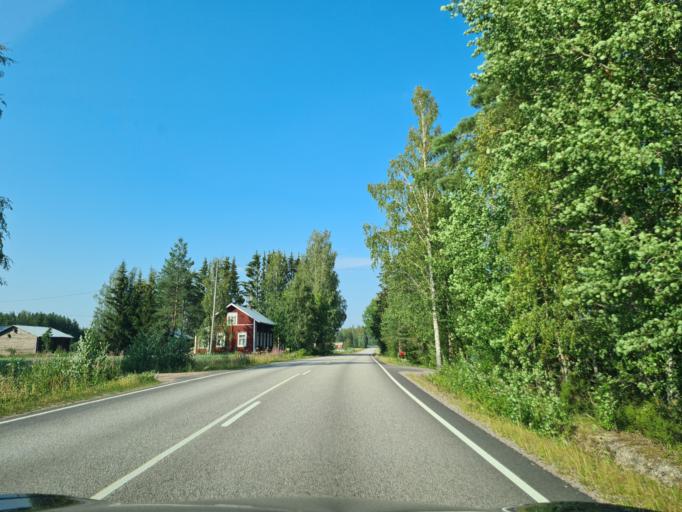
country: FI
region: Satakunta
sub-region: Pohjois-Satakunta
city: Karvia
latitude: 62.2189
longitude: 22.6067
